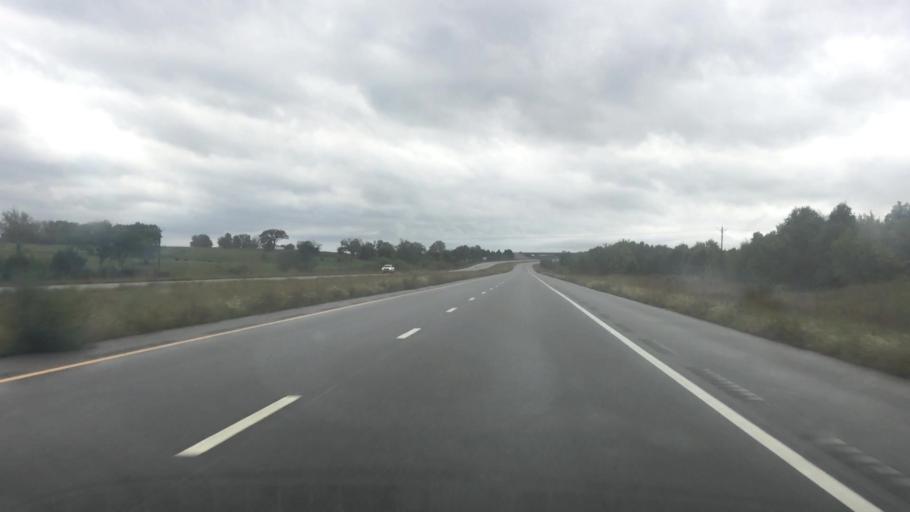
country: US
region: Kansas
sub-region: Miami County
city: Osawatomie
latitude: 38.4780
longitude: -94.9466
